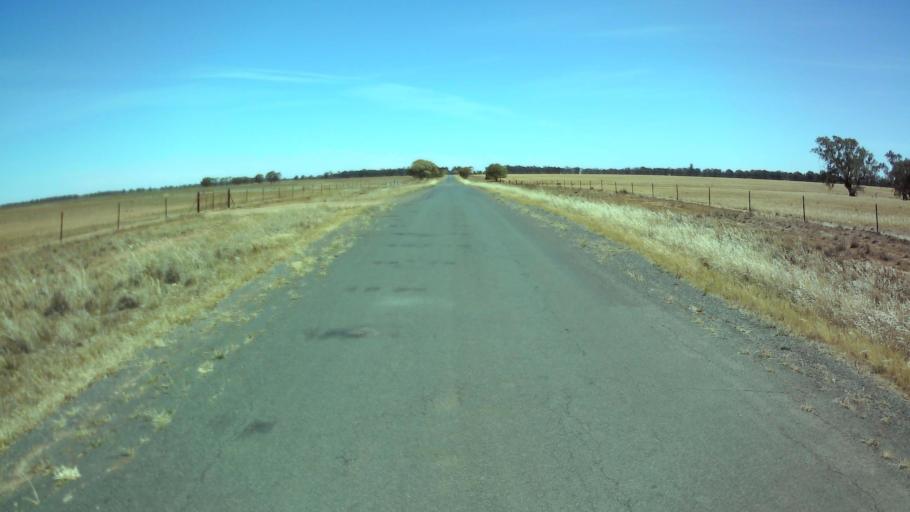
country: AU
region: New South Wales
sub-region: Weddin
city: Grenfell
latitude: -33.8507
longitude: 147.6956
